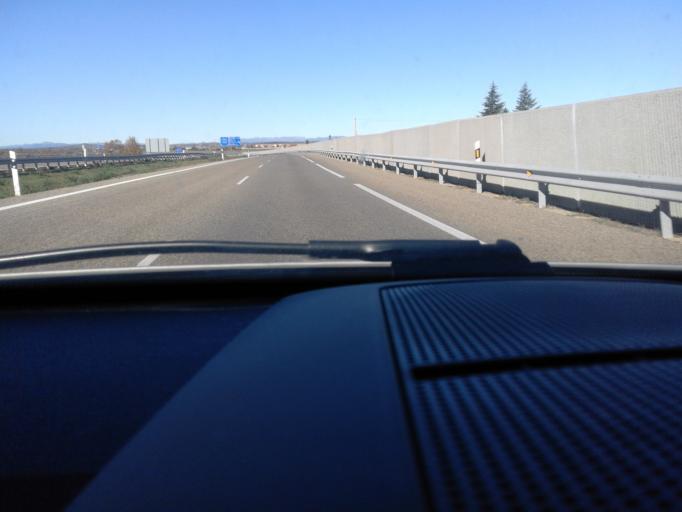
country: ES
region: Castille and Leon
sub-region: Provincia de Leon
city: Valverde de la Virgen
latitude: 42.5589
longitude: -5.6366
